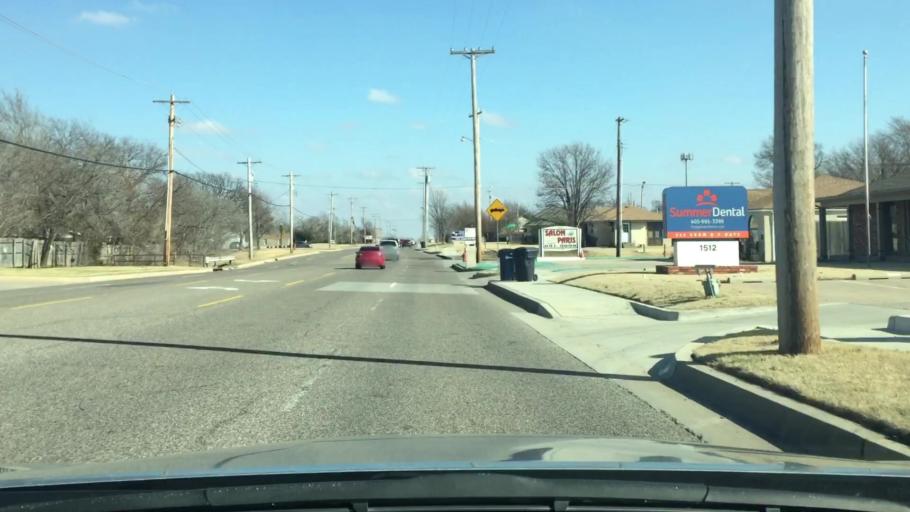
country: US
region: Oklahoma
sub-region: Cleveland County
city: Moore
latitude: 35.3771
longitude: -97.5442
